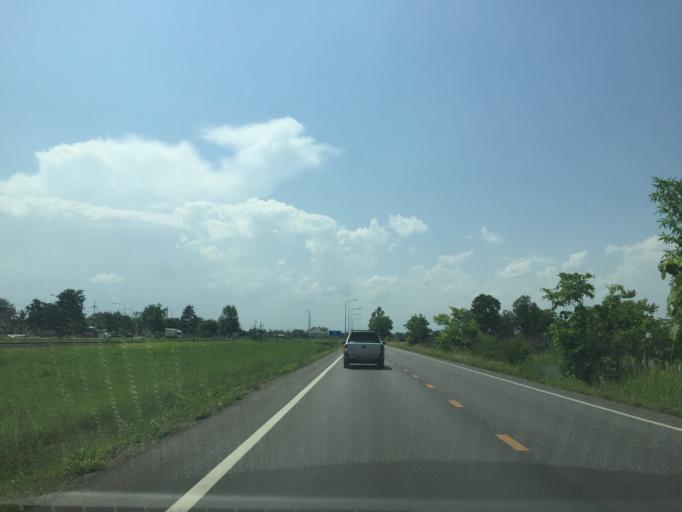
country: TH
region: Lamphun
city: Lamphun
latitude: 18.5734
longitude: 99.0288
